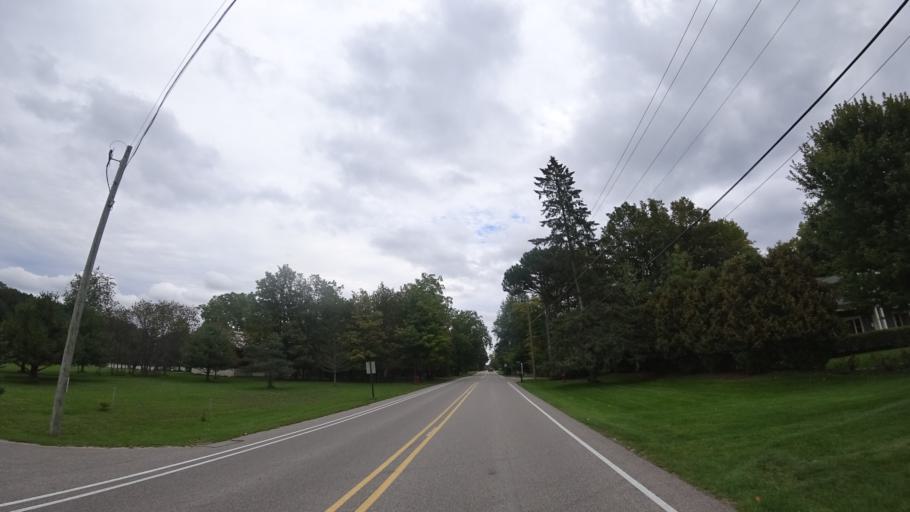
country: US
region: Michigan
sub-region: Emmet County
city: Harbor Springs
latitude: 45.4352
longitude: -85.0037
